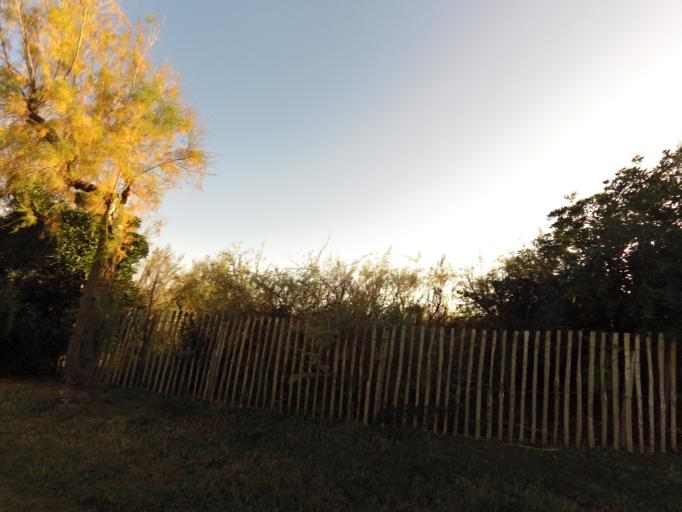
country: FR
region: Languedoc-Roussillon
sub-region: Departement de l'Herault
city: La Grande-Motte
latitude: 43.5584
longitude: 4.0624
